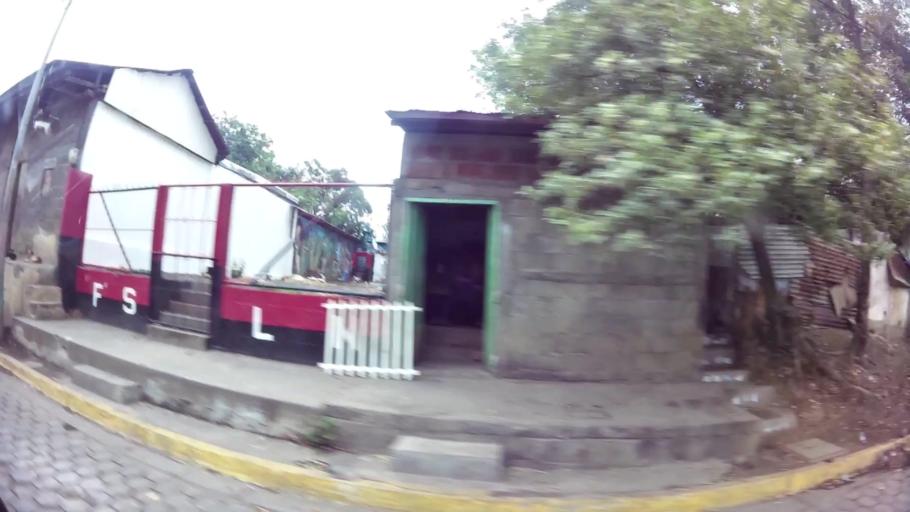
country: NI
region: Leon
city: Leon
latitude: 12.4479
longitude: -86.8766
